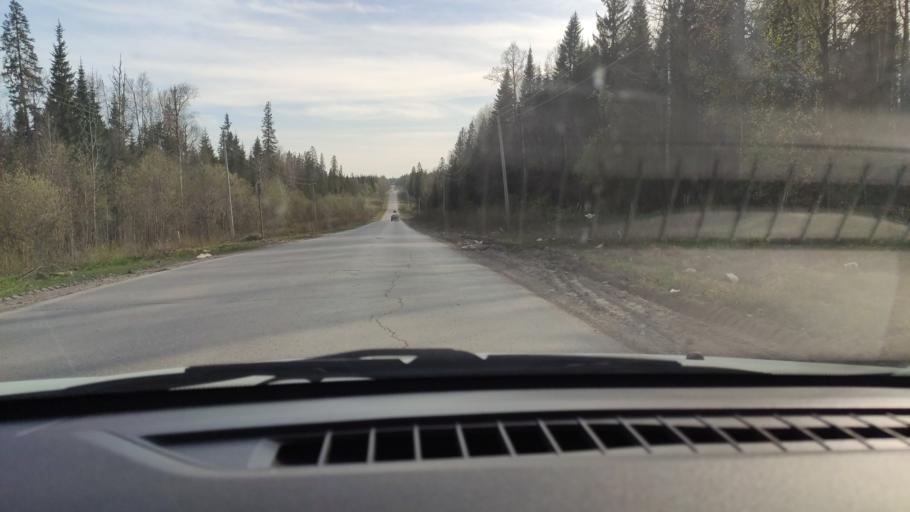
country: RU
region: Perm
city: Novyye Lyady
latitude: 57.9536
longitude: 56.5130
